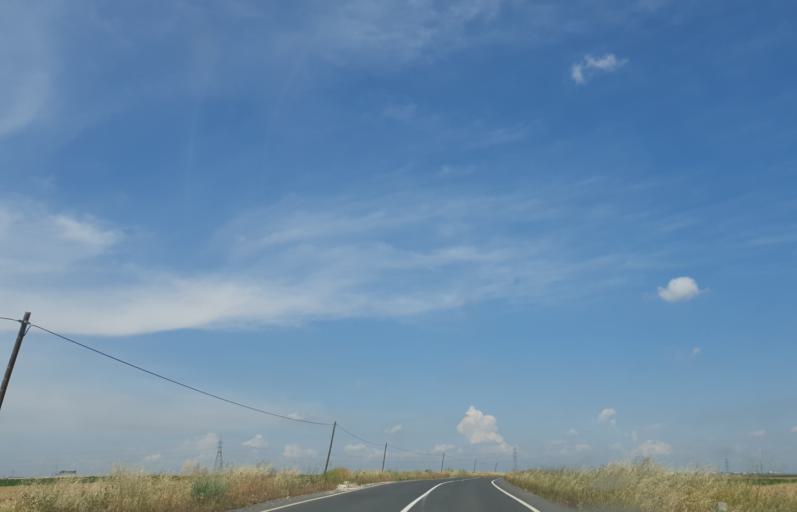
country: TR
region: Kirklareli
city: Buyukkaristiran
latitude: 41.2496
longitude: 27.6156
